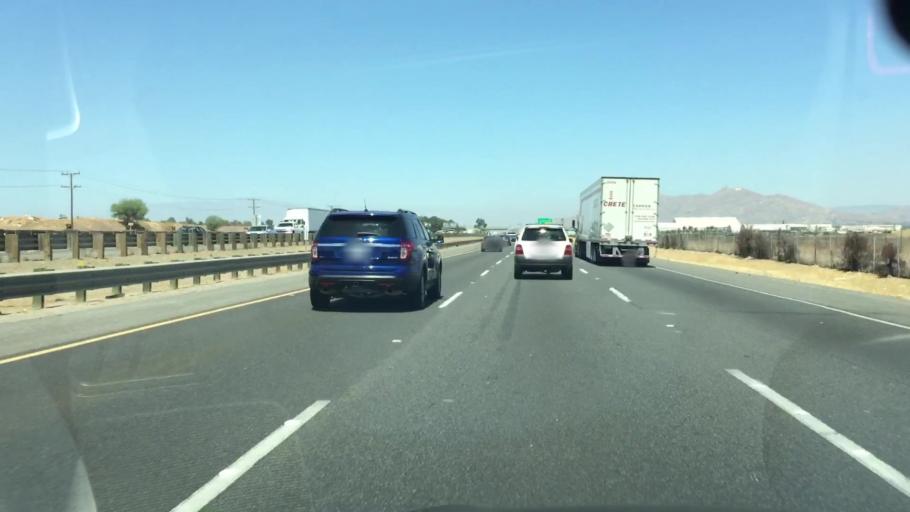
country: US
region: California
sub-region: Riverside County
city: March Air Force Base
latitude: 33.8757
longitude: -117.2648
